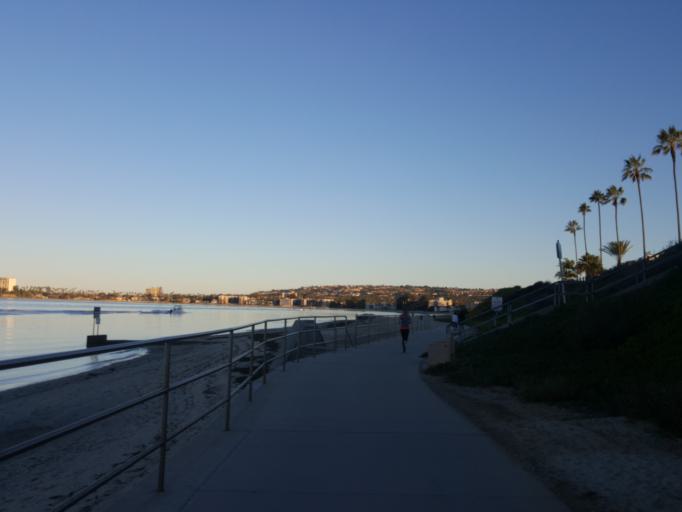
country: US
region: California
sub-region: San Diego County
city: La Jolla
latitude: 32.7818
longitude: -117.2392
